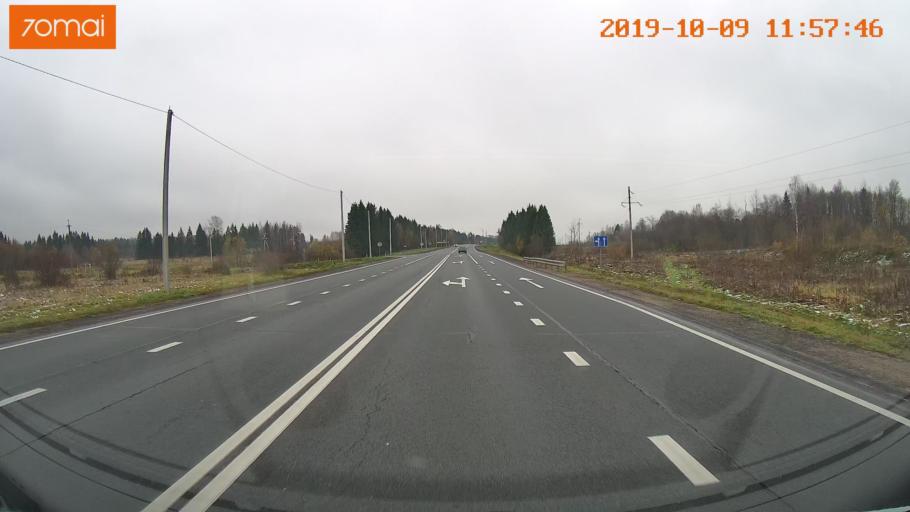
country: RU
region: Vologda
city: Gryazovets
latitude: 58.7278
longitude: 40.2945
